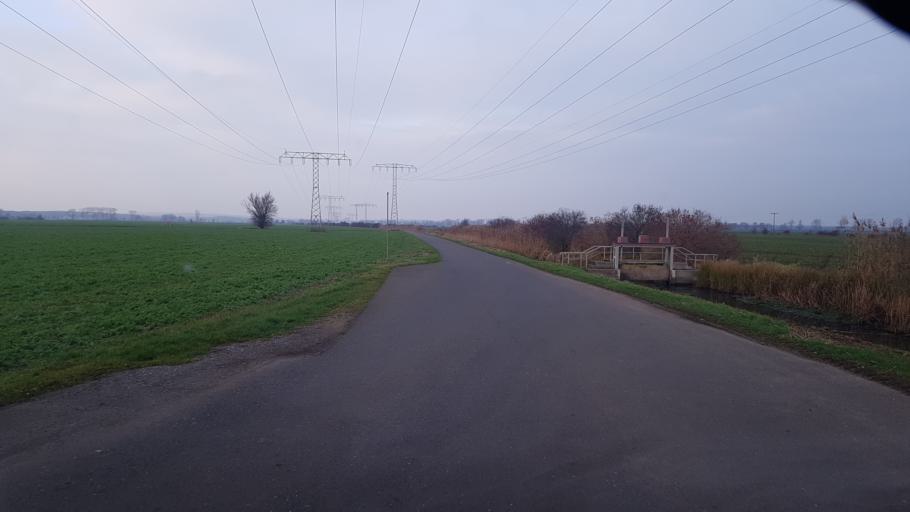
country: DE
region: Brandenburg
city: Ziltendorf
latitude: 52.2198
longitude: 14.6253
